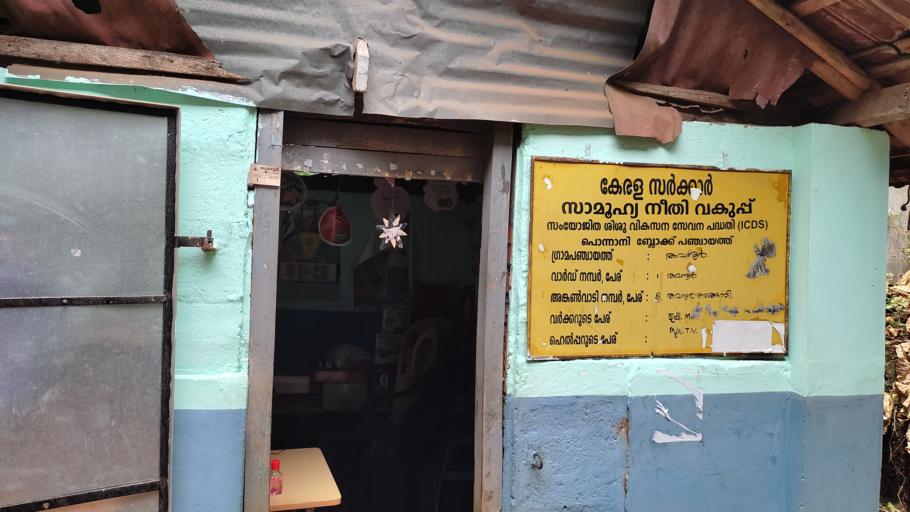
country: IN
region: Kerala
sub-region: Malappuram
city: Tirur
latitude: 10.8507
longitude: 75.9821
